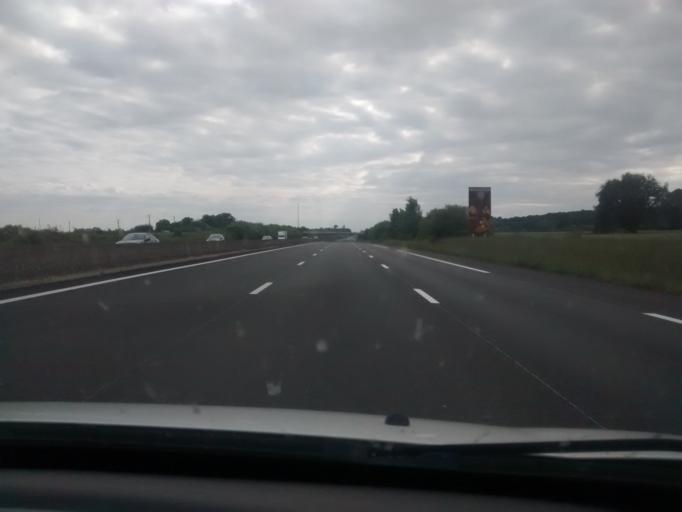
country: FR
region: Pays de la Loire
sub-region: Departement de la Sarthe
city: Tuffe
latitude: 48.1040
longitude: 0.5454
